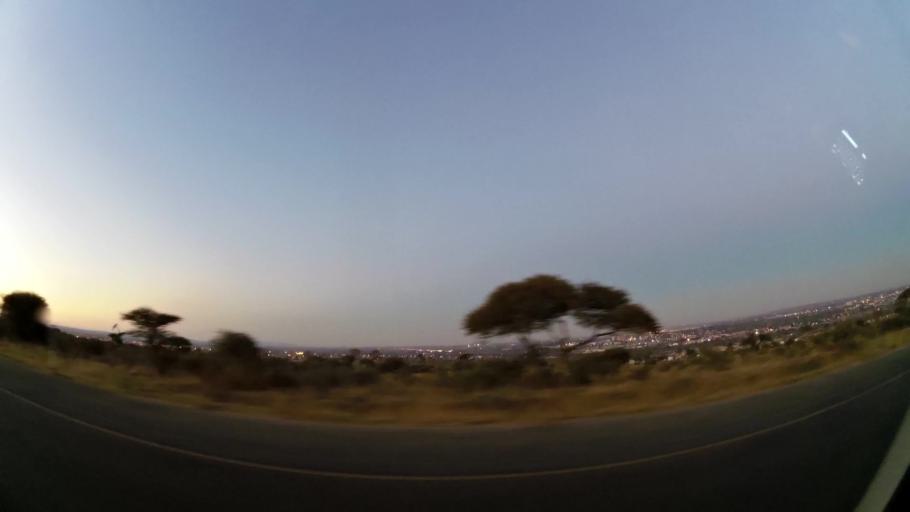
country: ZA
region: Limpopo
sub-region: Capricorn District Municipality
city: Polokwane
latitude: -23.8779
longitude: 29.4191
